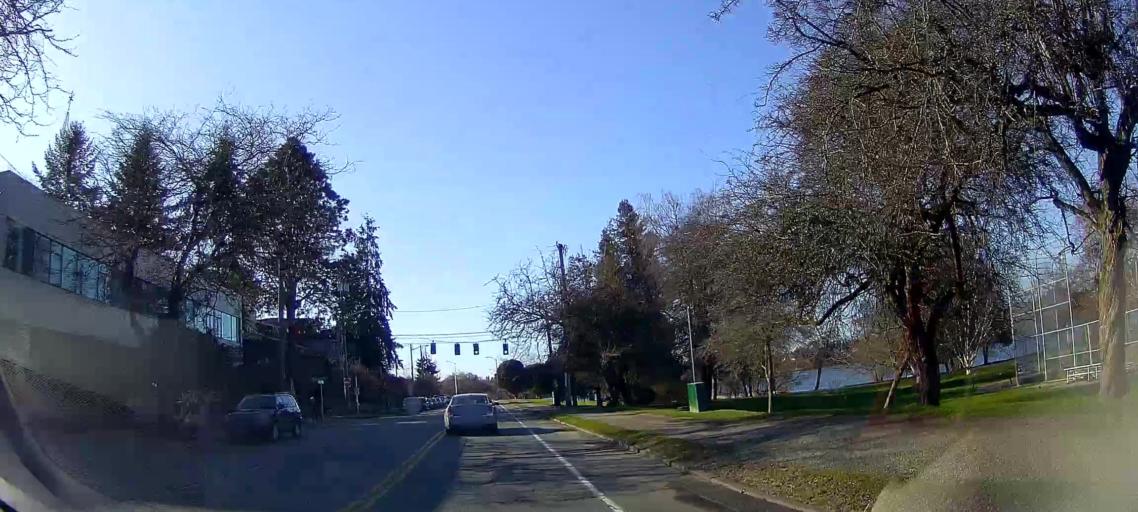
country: US
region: Washington
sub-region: King County
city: Seattle
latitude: 47.6784
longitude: -122.3283
